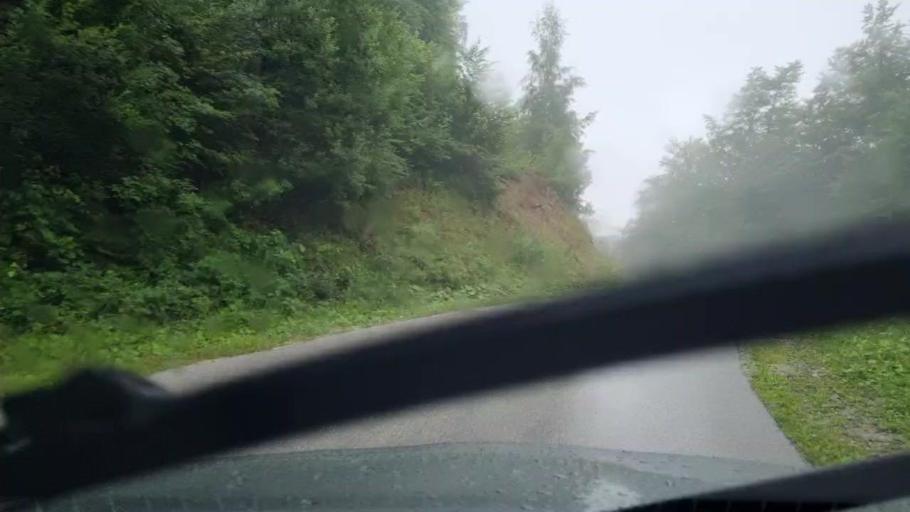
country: BA
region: Republika Srpska
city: Koran
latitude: 43.6558
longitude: 18.5940
